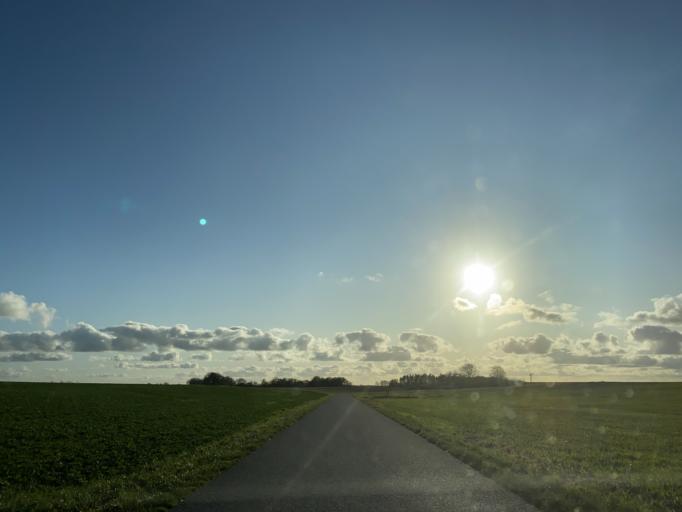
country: DK
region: Central Jutland
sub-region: Viborg Kommune
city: Bjerringbro
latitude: 56.3459
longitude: 9.7160
